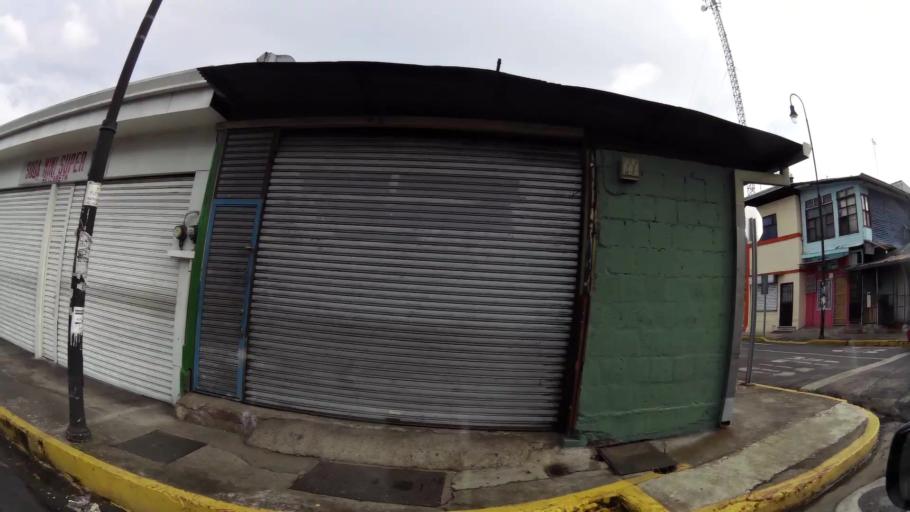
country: CR
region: San Jose
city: San Jose
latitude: 9.9387
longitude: -84.0848
